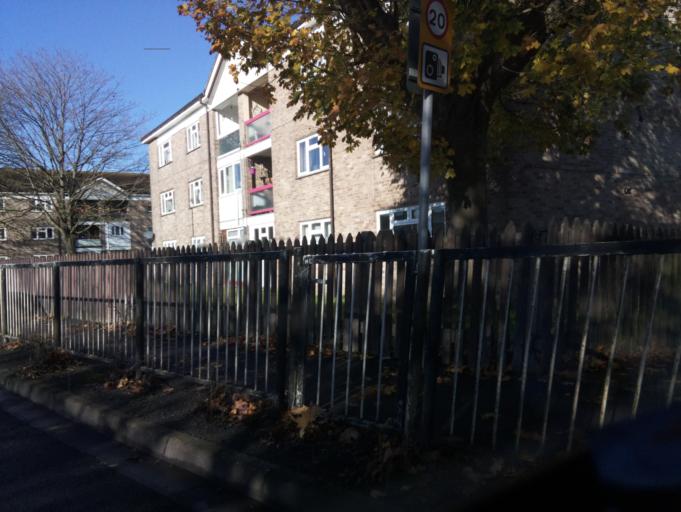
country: GB
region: England
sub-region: Somerset
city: Bridgwater
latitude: 51.1249
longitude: -2.9805
